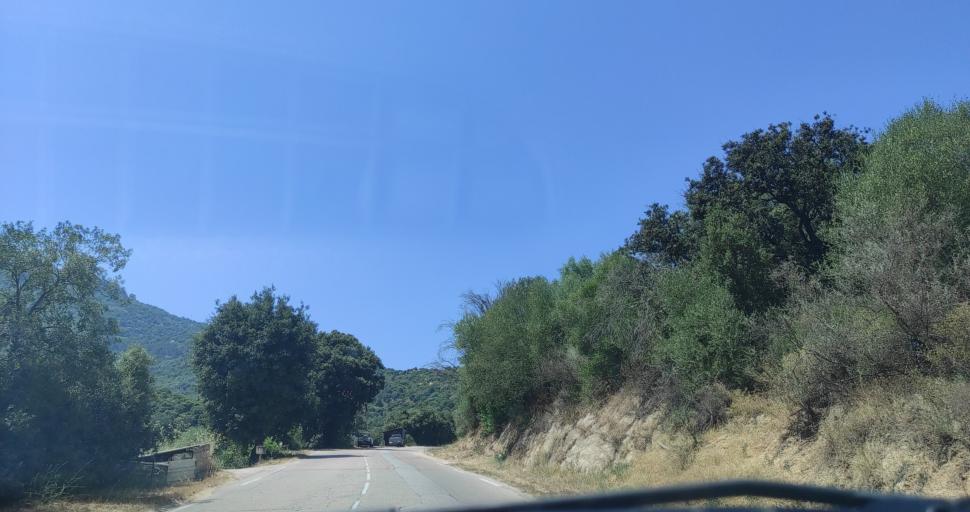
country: FR
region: Corsica
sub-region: Departement de la Corse-du-Sud
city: Alata
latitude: 41.9545
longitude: 8.7311
